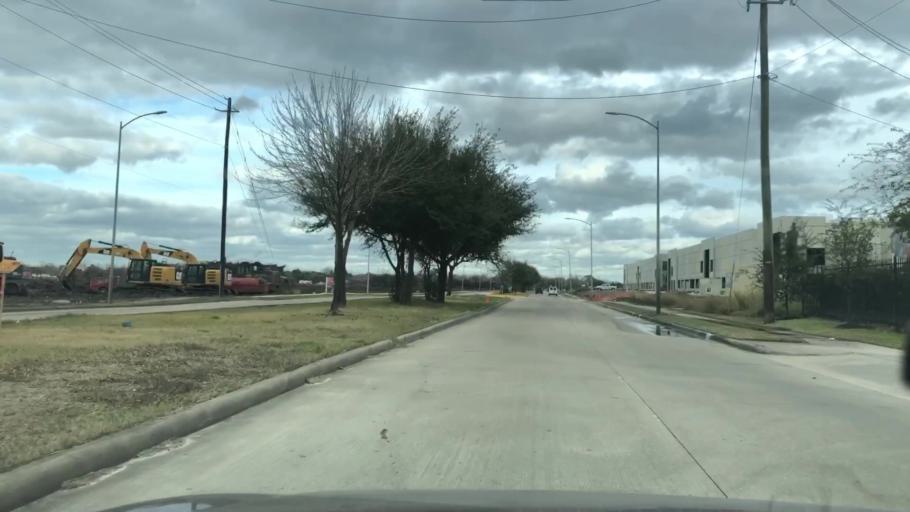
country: US
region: Texas
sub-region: Fort Bend County
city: Missouri City
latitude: 29.6074
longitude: -95.4750
